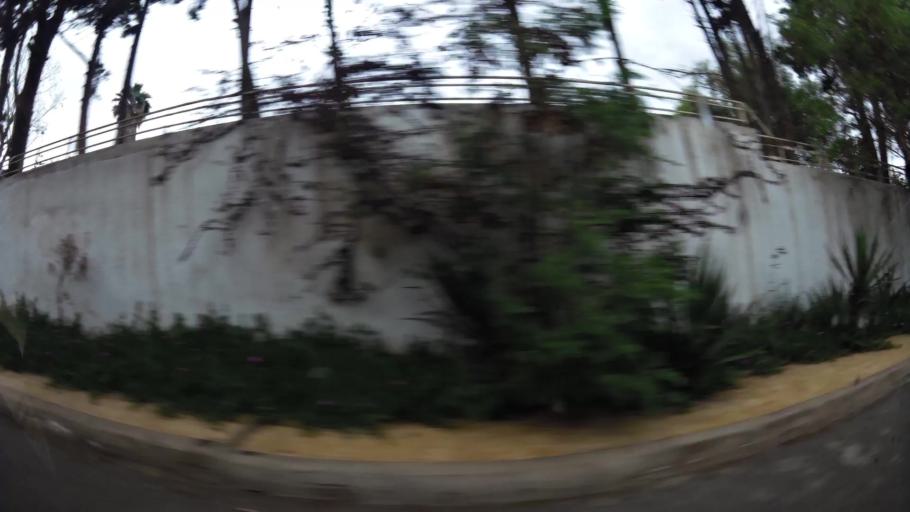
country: MA
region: Grand Casablanca
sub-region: Casablanca
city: Casablanca
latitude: 33.5288
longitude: -7.6344
